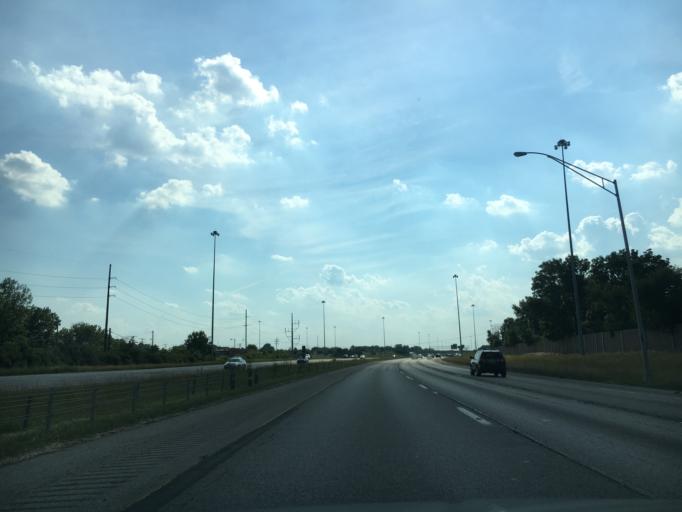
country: US
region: Ohio
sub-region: Franklin County
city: Whitehall
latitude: 39.9322
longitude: -82.9073
